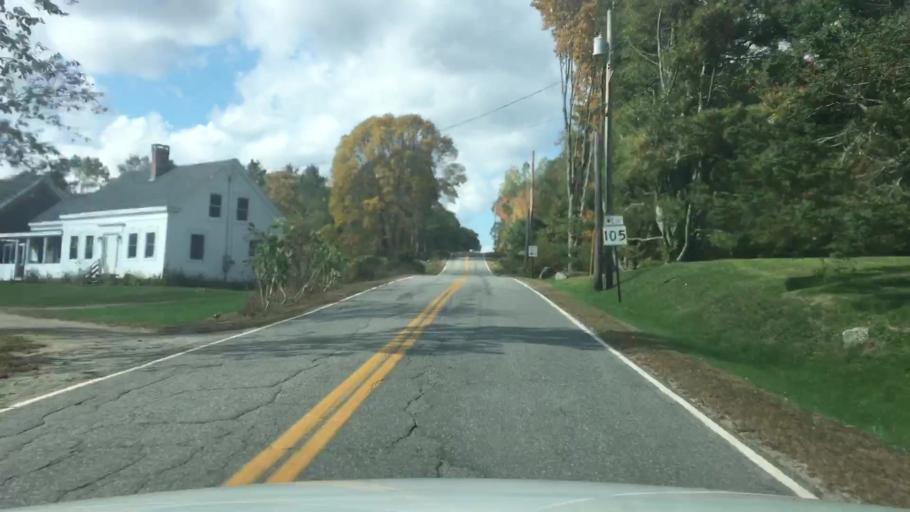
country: US
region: Maine
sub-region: Knox County
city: Washington
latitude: 44.2985
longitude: -69.3184
